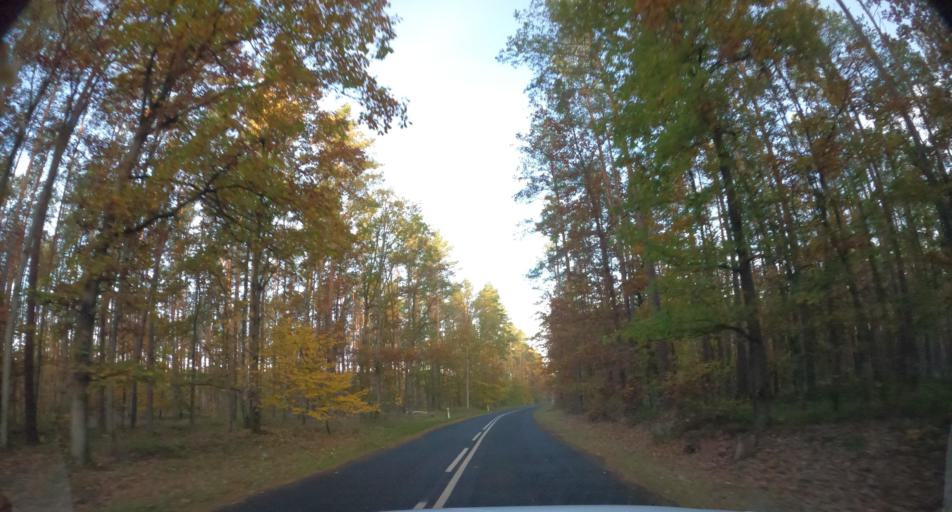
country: PL
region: West Pomeranian Voivodeship
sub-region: Powiat policki
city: Nowe Warpno
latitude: 53.6068
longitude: 14.3180
